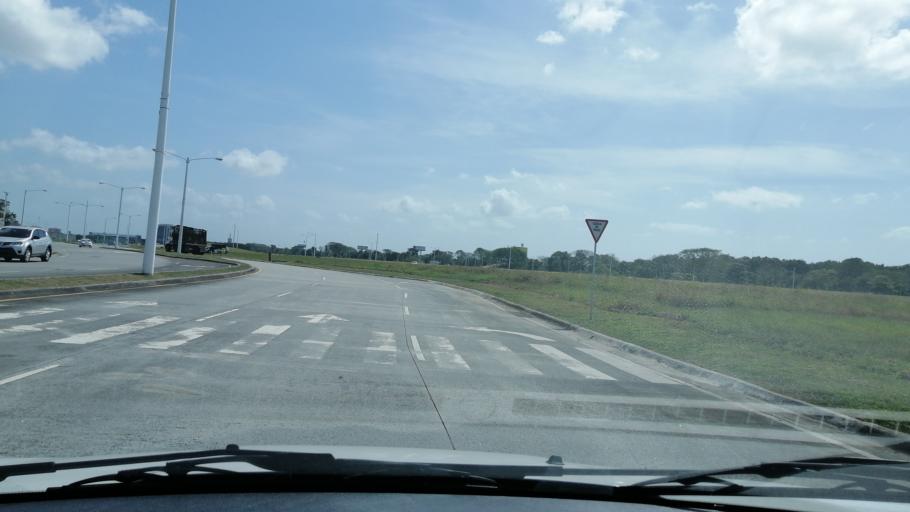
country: PA
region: Panama
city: San Miguelito
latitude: 9.0382
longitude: -79.4358
